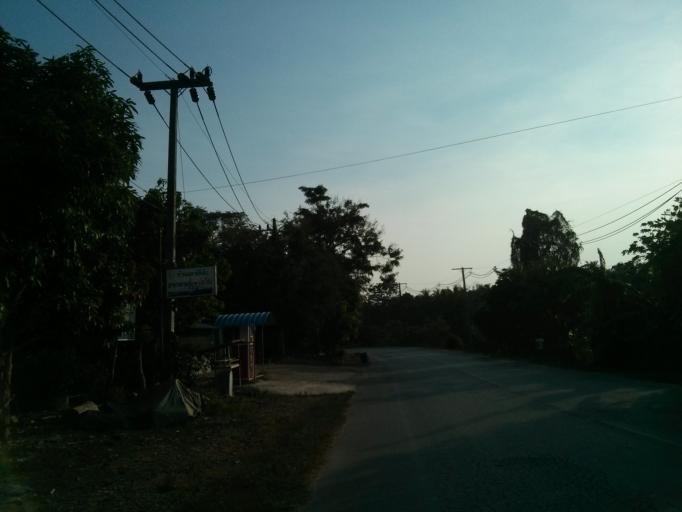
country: TH
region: Krabi
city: Saladan
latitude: 7.5644
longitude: 99.0396
